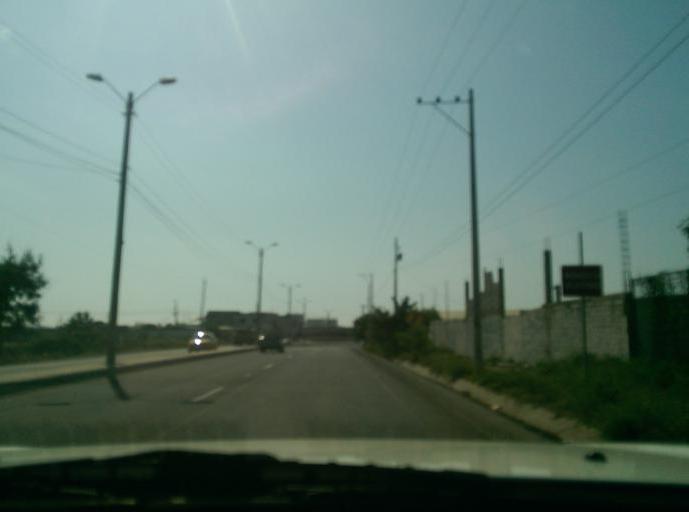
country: EC
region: Manabi
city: Manta
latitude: -0.9982
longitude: -80.7073
